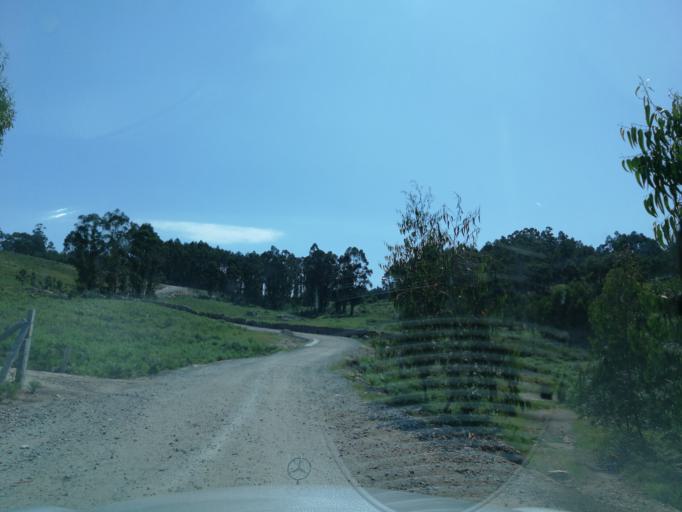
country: PT
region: Braga
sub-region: Braga
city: Adaufe
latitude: 41.5617
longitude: -8.3448
